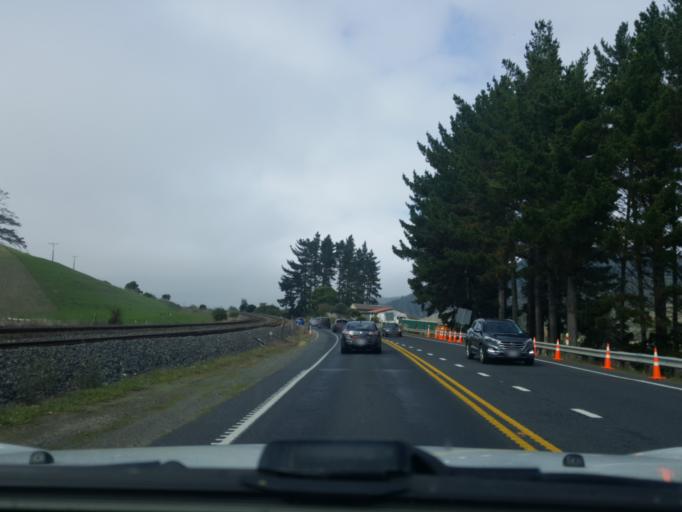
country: NZ
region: Waikato
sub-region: Waikato District
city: Ngaruawahia
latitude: -37.5980
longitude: 175.1634
